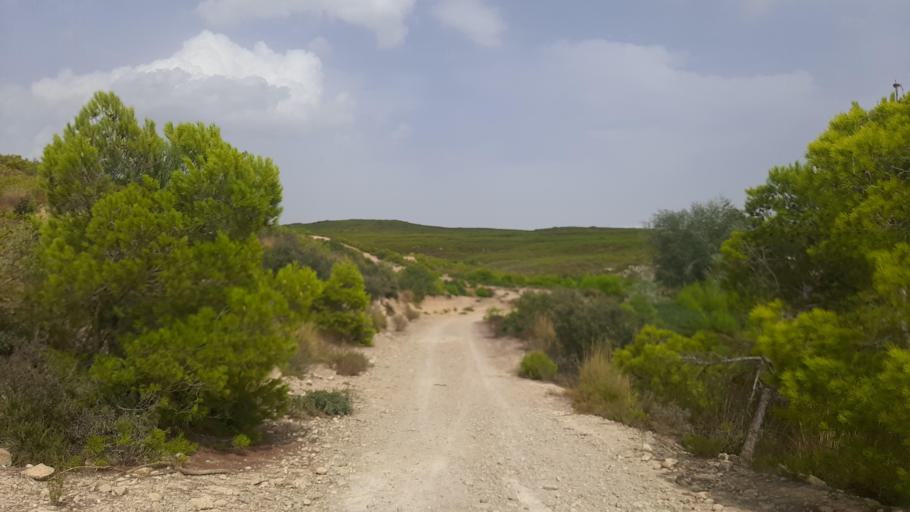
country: TN
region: Zaghwan
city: El Fahs
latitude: 36.1962
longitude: 9.8488
